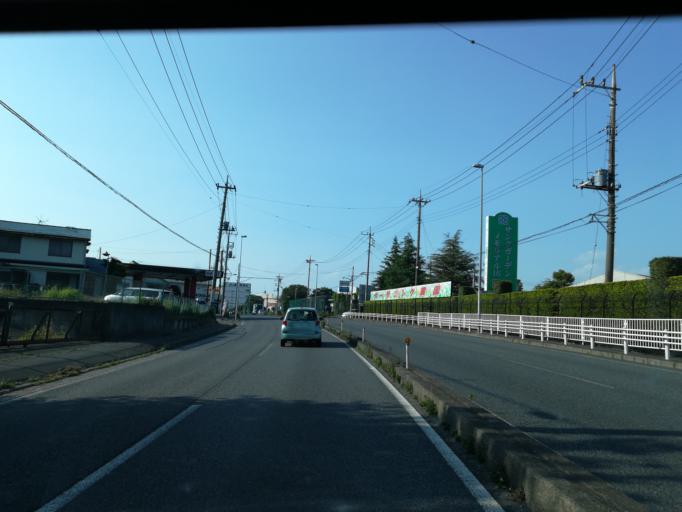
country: JP
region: Saitama
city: Sayama
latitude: 35.8069
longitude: 139.3790
